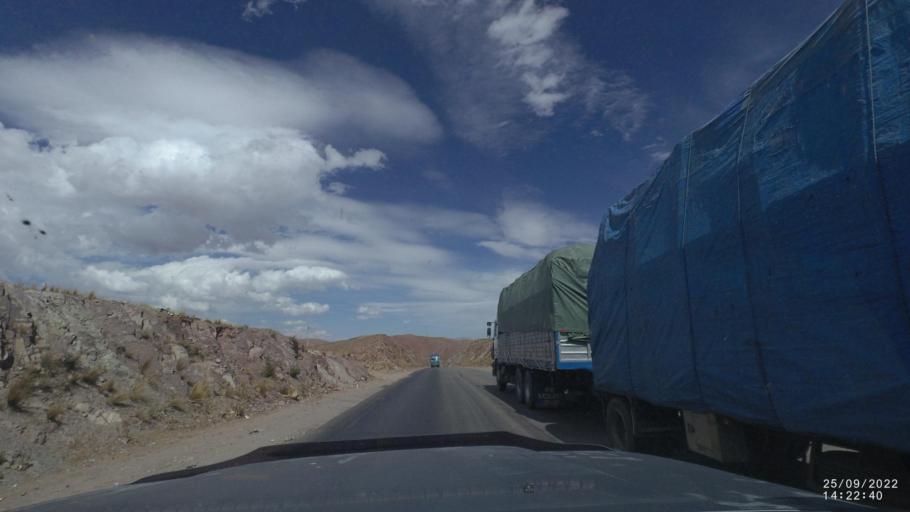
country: BO
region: Cochabamba
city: Colchani
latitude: -17.6814
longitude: -66.7273
